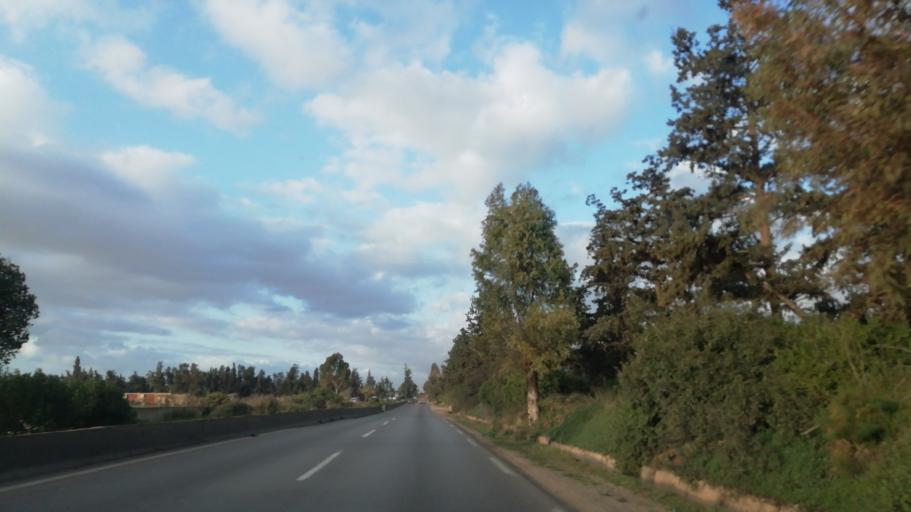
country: DZ
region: Oran
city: Bou Tlelis
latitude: 35.5959
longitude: -0.7843
